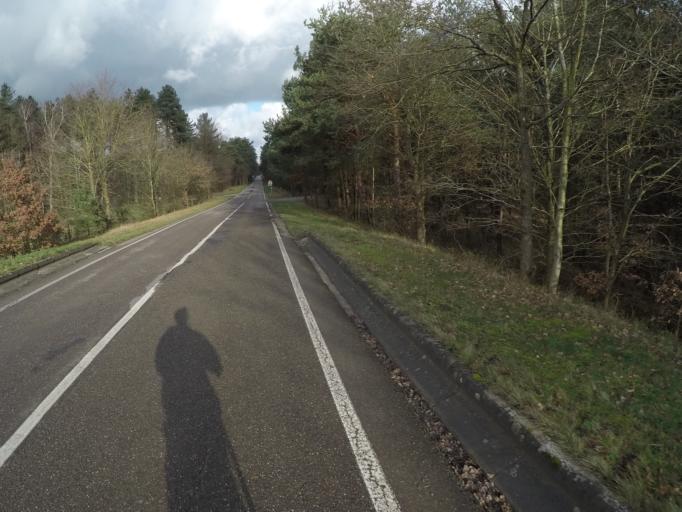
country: BE
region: Flanders
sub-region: Provincie Antwerpen
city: Vorselaar
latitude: 51.2477
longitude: 4.7750
